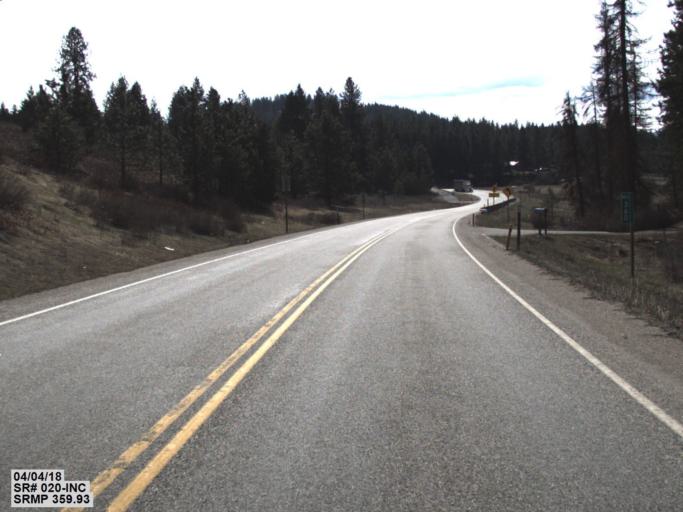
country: US
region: Washington
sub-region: Stevens County
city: Colville
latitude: 48.5179
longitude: -117.8084
